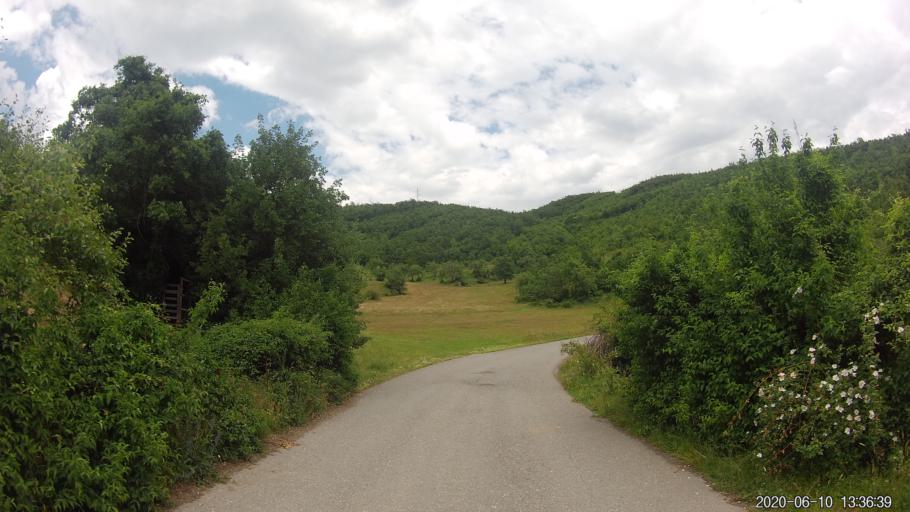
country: XK
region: Prizren
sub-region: Komuna e Therandes
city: Budakovo
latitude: 42.4118
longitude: 20.8996
